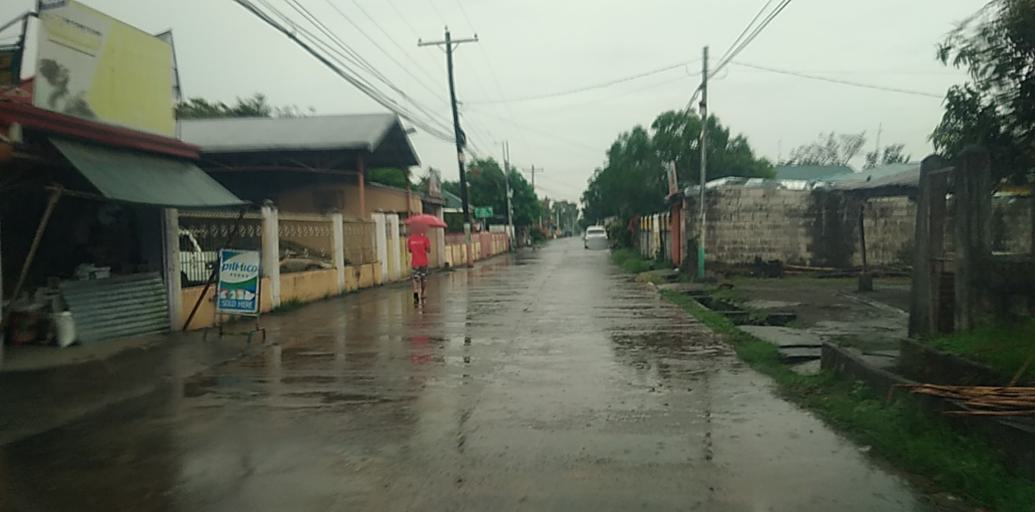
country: PH
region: Central Luzon
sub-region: Province of Pampanga
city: Arenas
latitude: 15.1712
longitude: 120.6846
